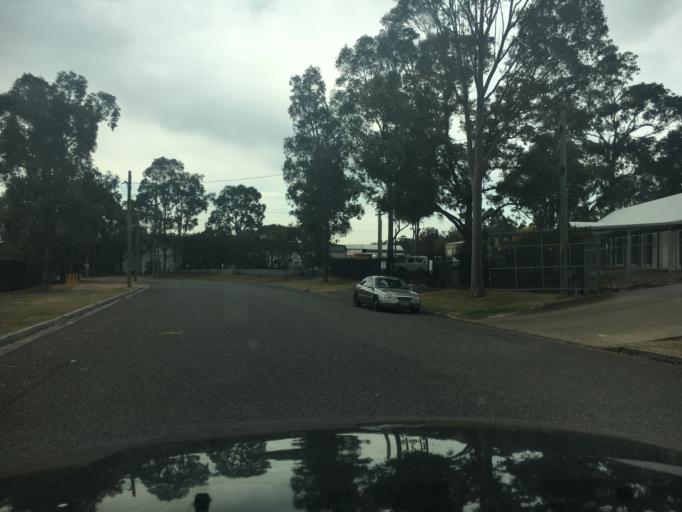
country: AU
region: New South Wales
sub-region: Maitland Municipality
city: East Maitland
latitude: -32.7619
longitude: 151.5986
